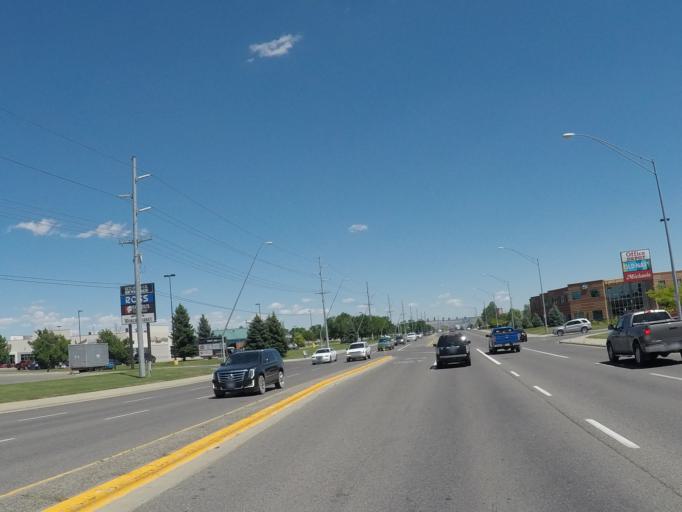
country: US
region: Montana
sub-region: Yellowstone County
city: Billings
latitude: 45.7552
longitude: -108.5846
